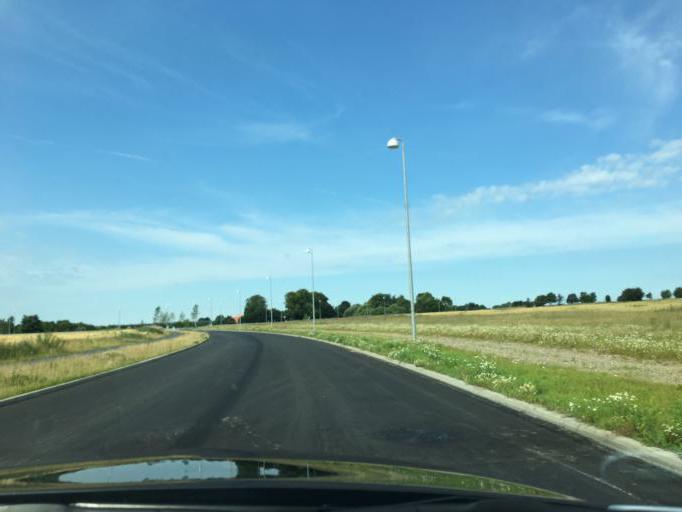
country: DK
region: South Denmark
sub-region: Kolding Kommune
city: Kolding
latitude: 55.5449
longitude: 9.4509
